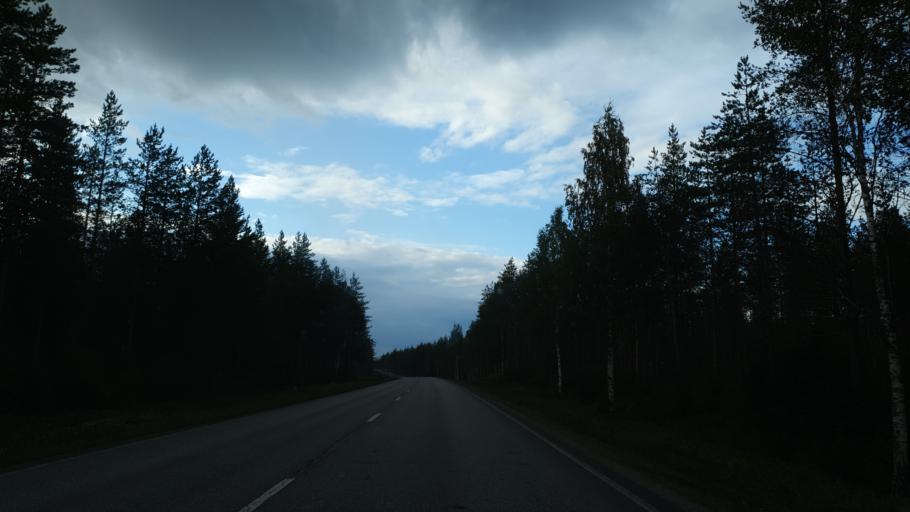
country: FI
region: North Karelia
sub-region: Pielisen Karjala
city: Lieksa
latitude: 63.1752
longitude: 30.1488
